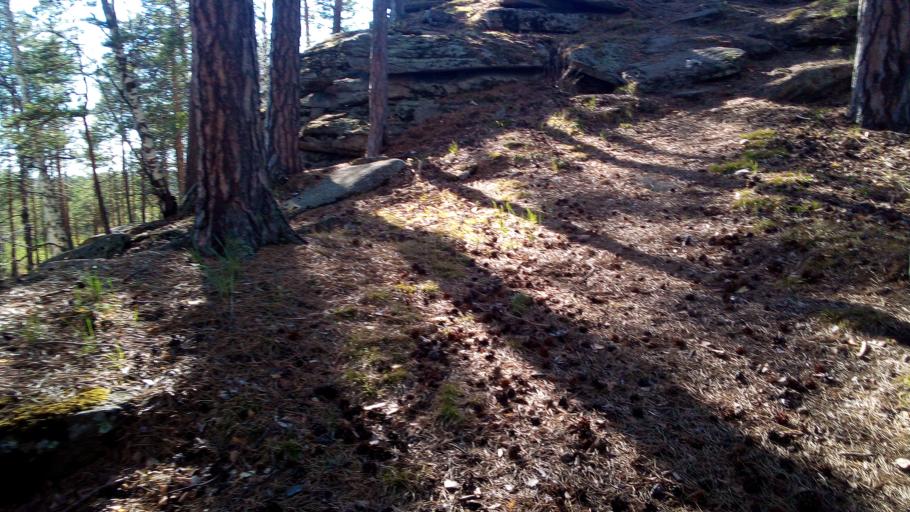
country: RU
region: Chelyabinsk
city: Chebarkul'
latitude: 55.1139
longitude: 60.3329
